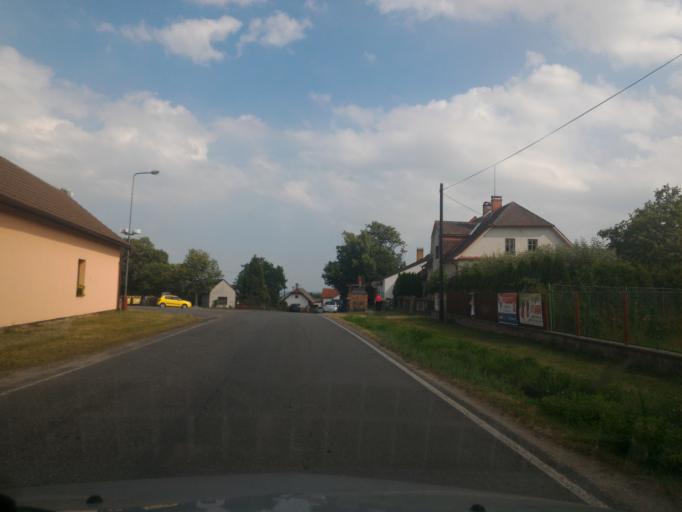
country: CZ
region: Central Bohemia
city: Loucen
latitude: 50.2735
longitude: 15.0135
